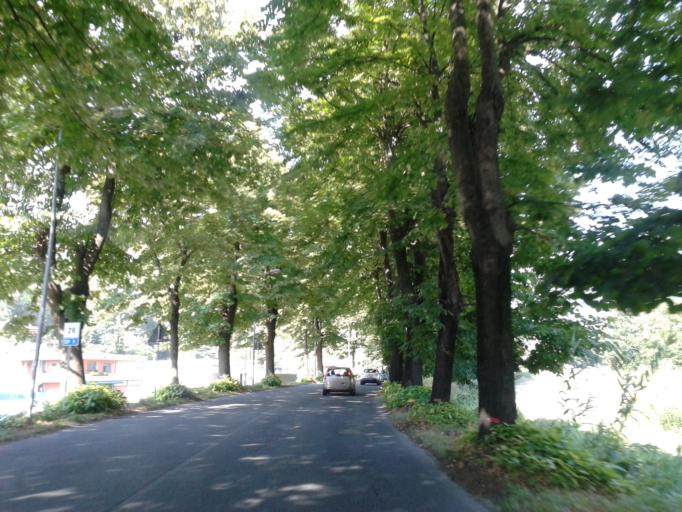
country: IT
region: Tuscany
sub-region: Provincia di Lucca
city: Piano di Mommio
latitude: 43.9344
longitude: 10.2816
